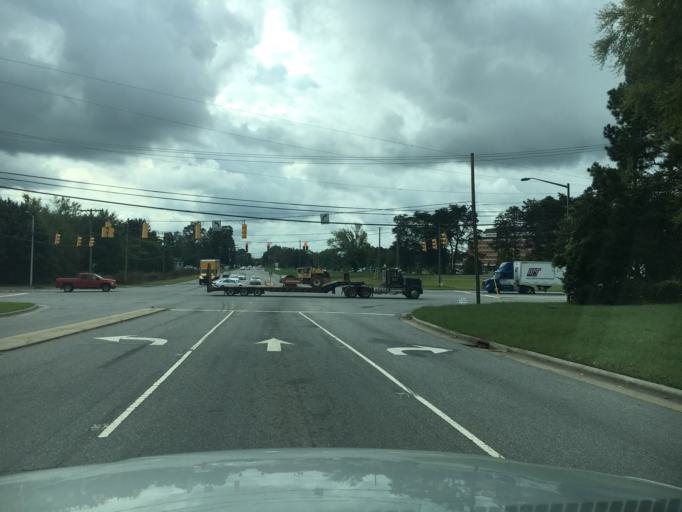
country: US
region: North Carolina
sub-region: Catawba County
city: Saint Stephens
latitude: 35.7178
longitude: -81.2657
